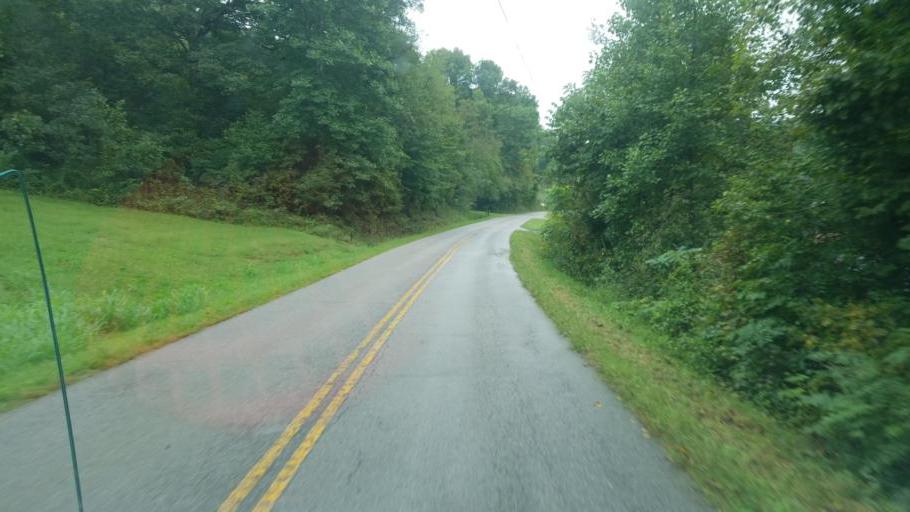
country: US
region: Kentucky
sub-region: Fleming County
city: Flemingsburg
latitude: 38.3812
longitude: -83.5415
